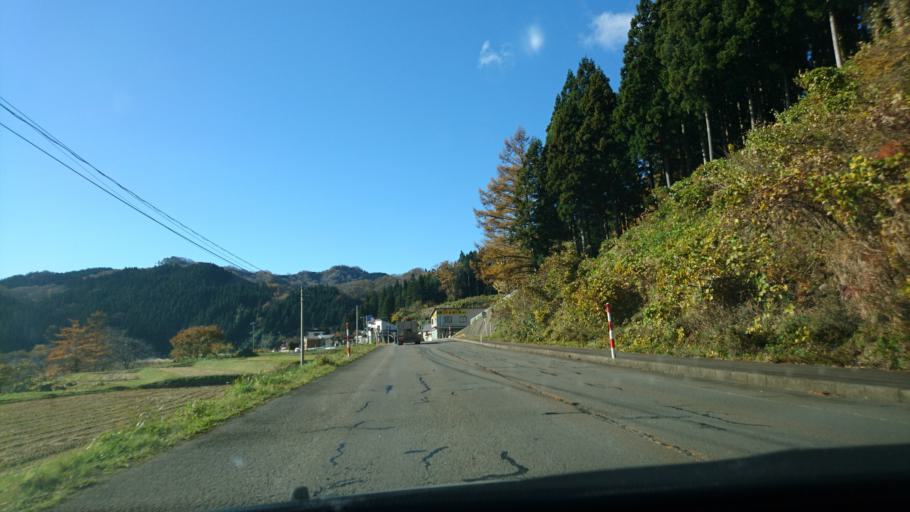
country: JP
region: Akita
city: Omagari
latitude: 39.3258
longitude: 140.1815
